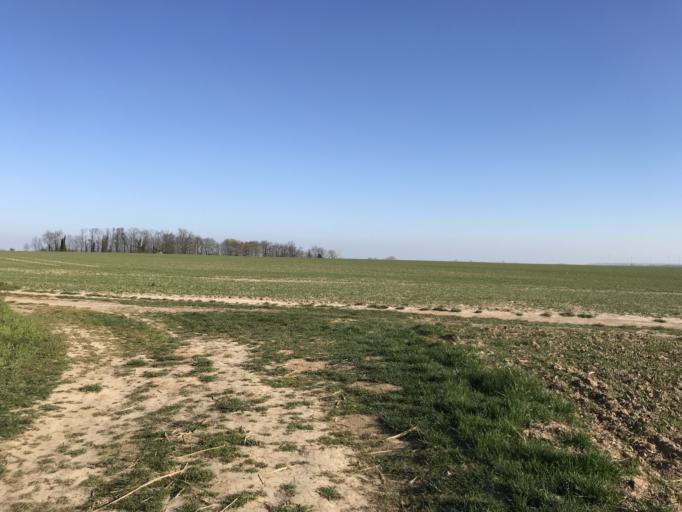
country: DE
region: Rheinland-Pfalz
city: Stadecken-Elsheim
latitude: 49.9307
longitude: 8.1187
